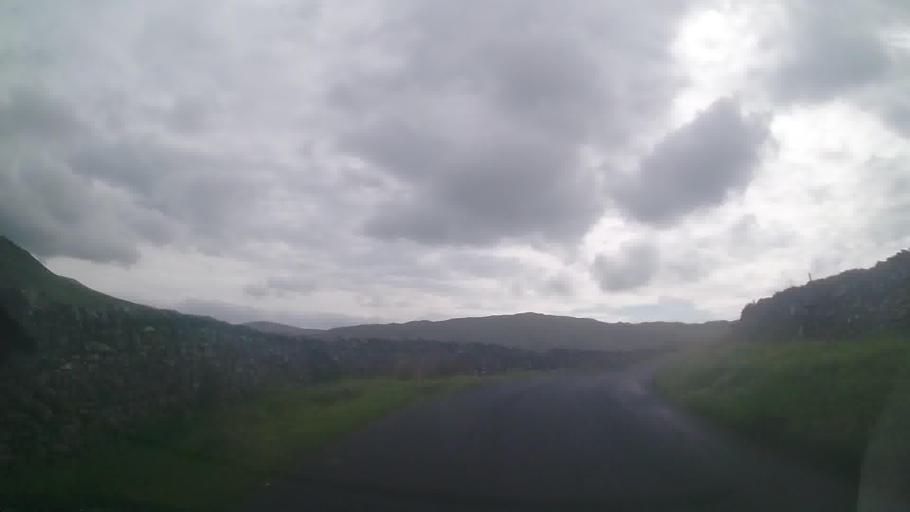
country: GB
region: England
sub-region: Cumbria
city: Ambleside
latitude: 54.4574
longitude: -2.9335
